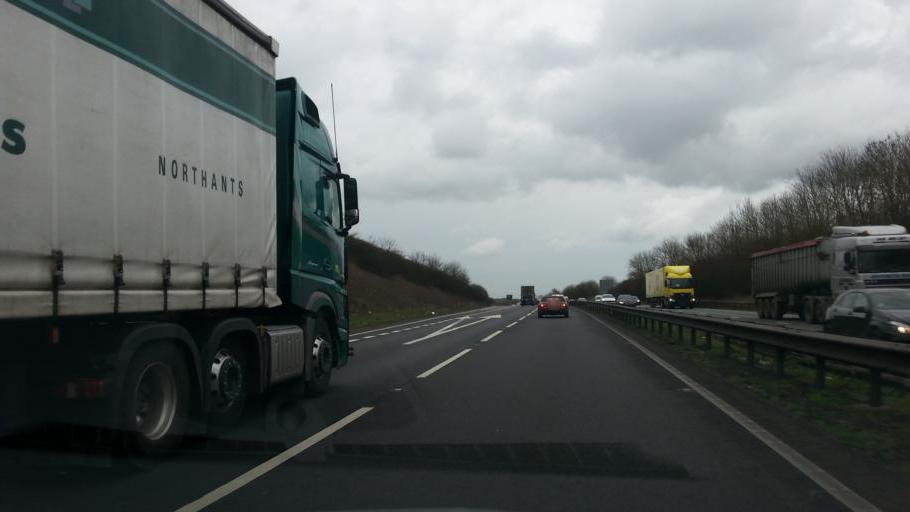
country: GB
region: England
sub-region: Northamptonshire
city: Brixworth
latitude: 52.4000
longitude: -0.9254
